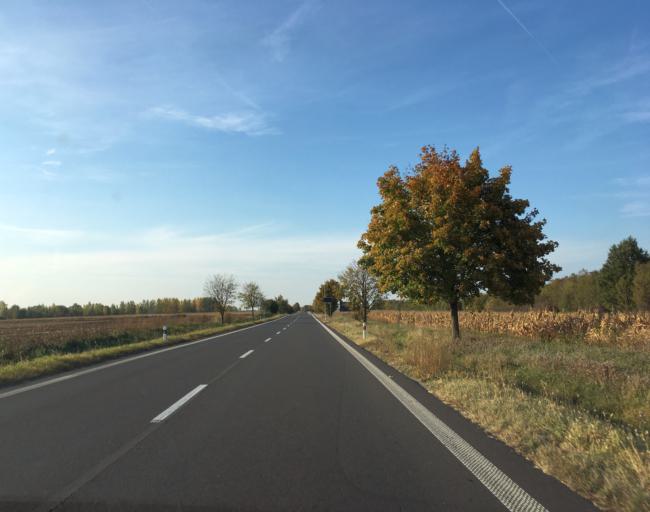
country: SK
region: Nitriansky
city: Surany
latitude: 48.0725
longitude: 18.0888
